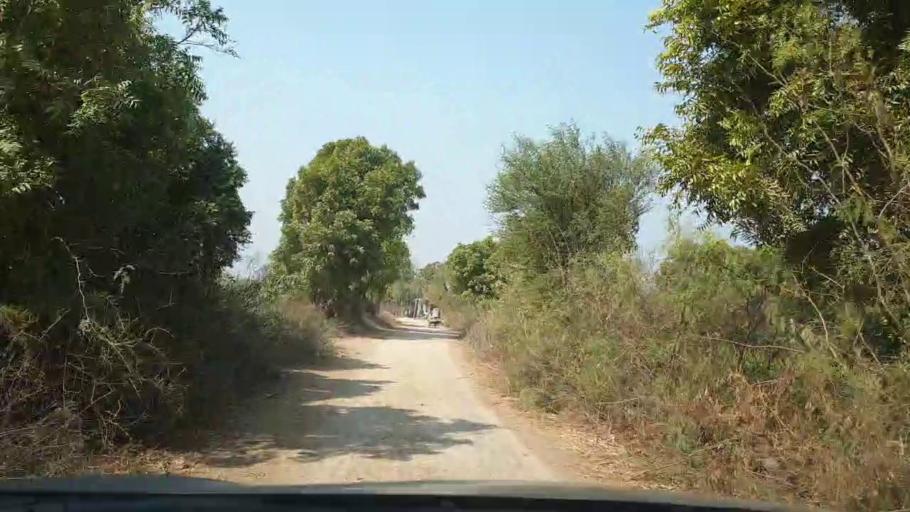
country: PK
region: Sindh
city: Tando Allahyar
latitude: 25.5308
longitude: 68.7673
